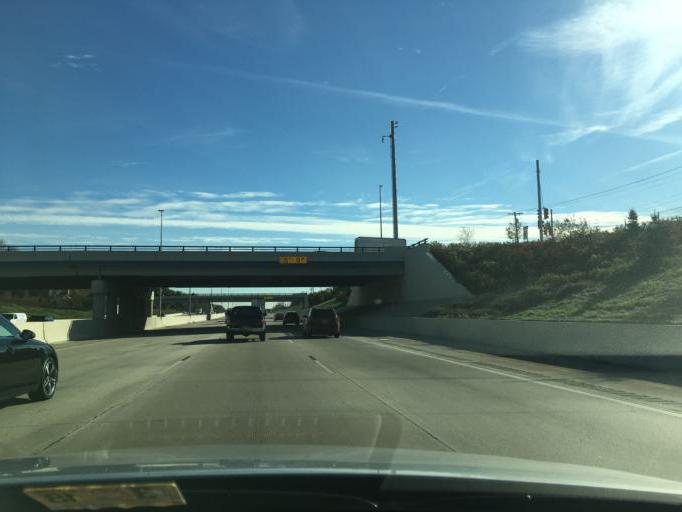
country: US
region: Michigan
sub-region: Wayne County
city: Livonia
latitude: 42.3828
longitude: -83.3545
